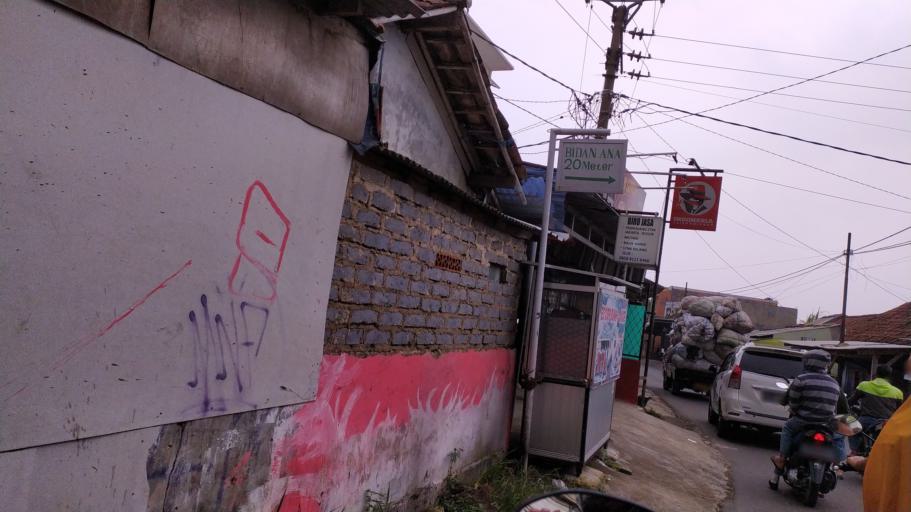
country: ID
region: West Java
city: Ciampea
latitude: -6.6042
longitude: 106.7018
